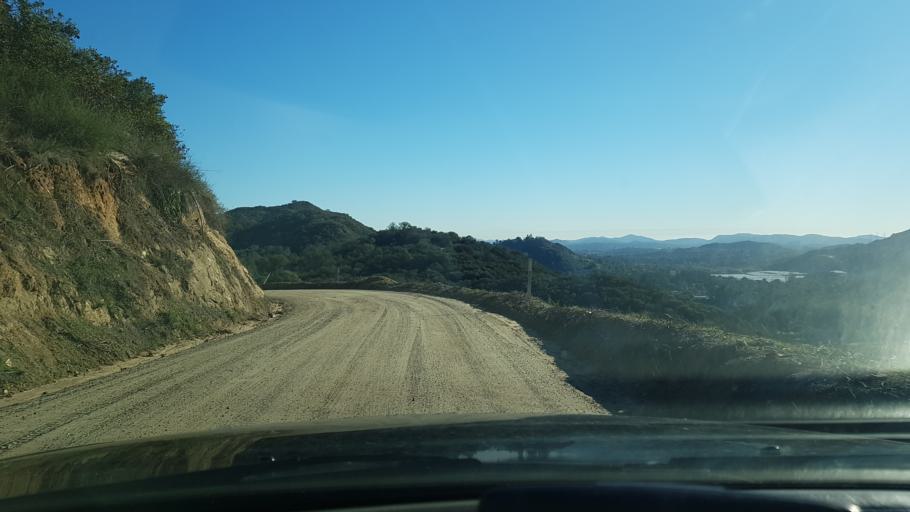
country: US
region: California
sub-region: San Diego County
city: Hidden Meadows
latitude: 33.2123
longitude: -117.0875
